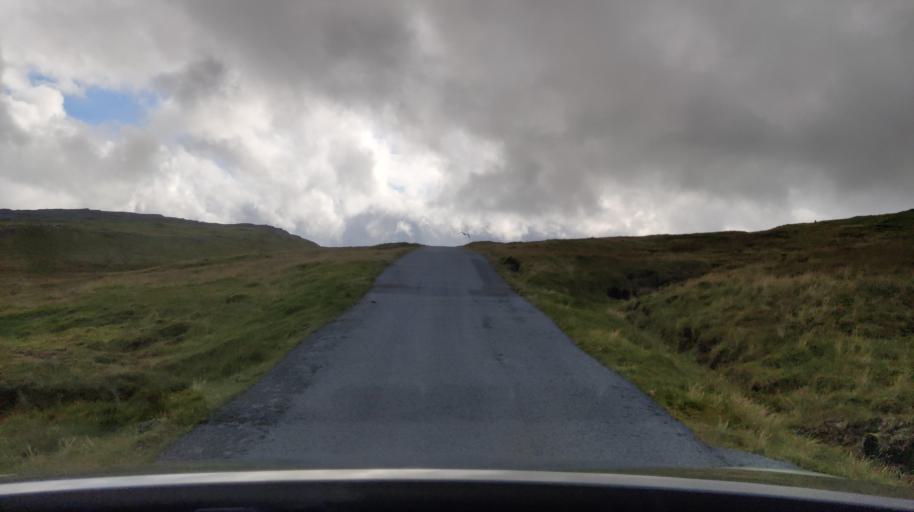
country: FO
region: Streymoy
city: Vestmanna
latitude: 62.1712
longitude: -7.1597
